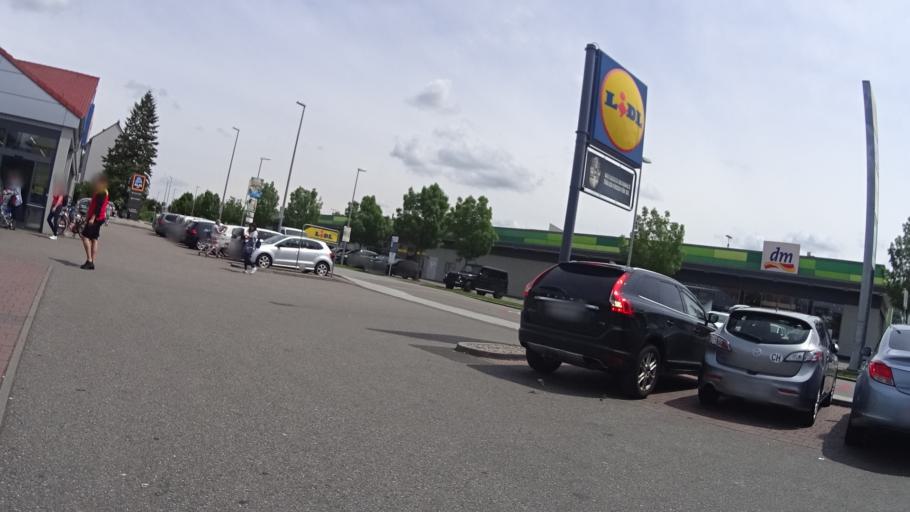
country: DE
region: Baden-Wuerttemberg
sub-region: Freiburg Region
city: Rheinfelden (Baden)
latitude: 47.5572
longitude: 7.7813
